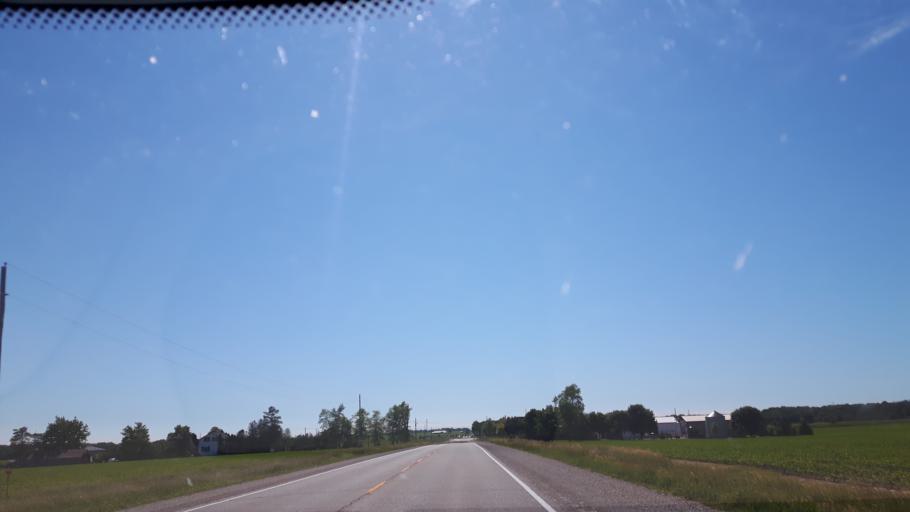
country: CA
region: Ontario
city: Bluewater
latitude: 43.4270
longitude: -81.5688
